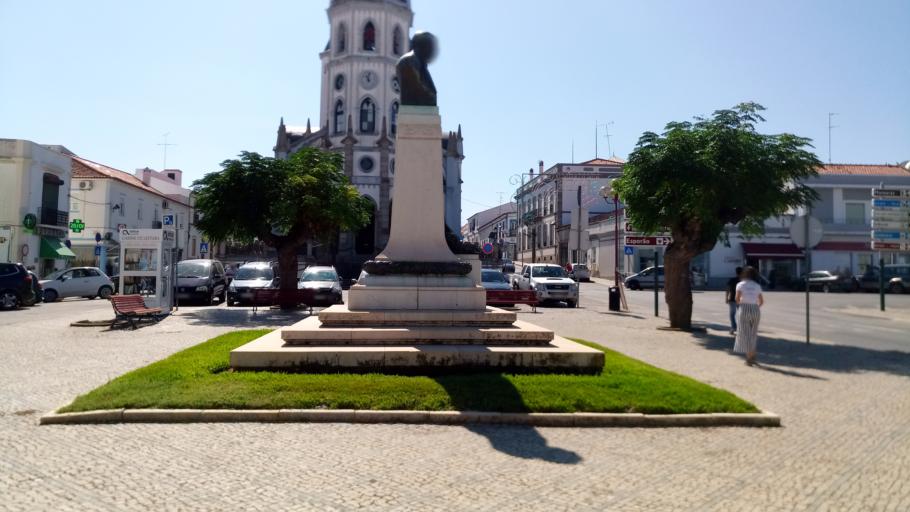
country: PT
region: Evora
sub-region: Reguengos de Monsaraz
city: Reguengos de Monsaraz
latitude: 38.4245
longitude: -7.5348
